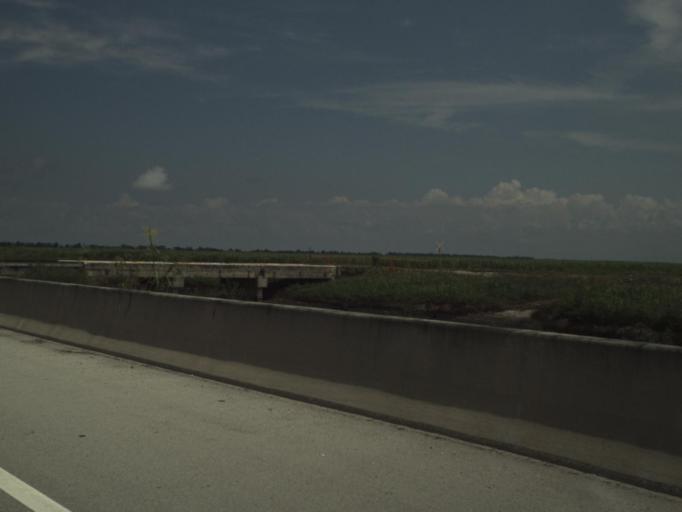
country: US
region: Florida
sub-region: Palm Beach County
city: Pahokee
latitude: 26.8465
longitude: -80.6078
